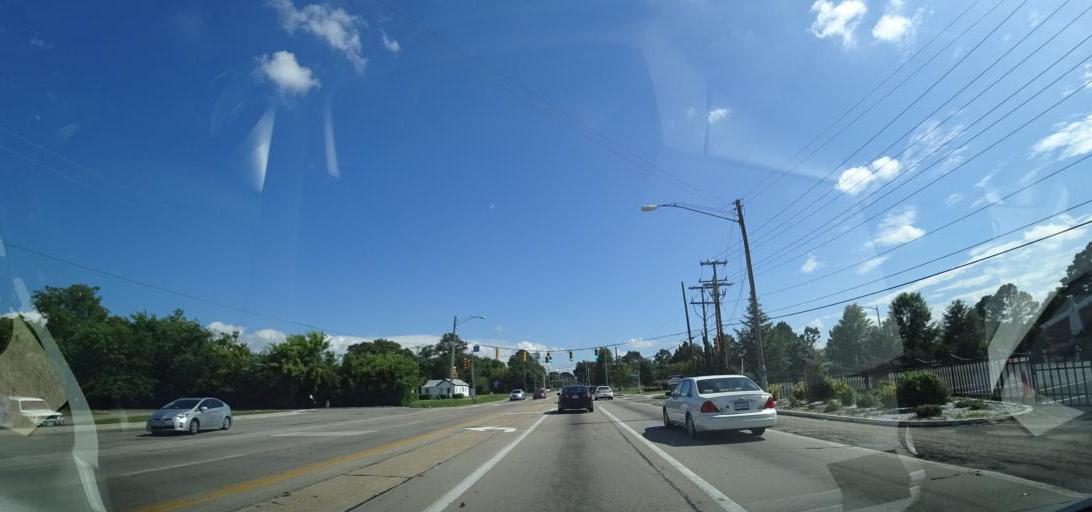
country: US
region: Virginia
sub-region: City of Hampton
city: Hampton
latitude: 37.0308
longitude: -76.3629
